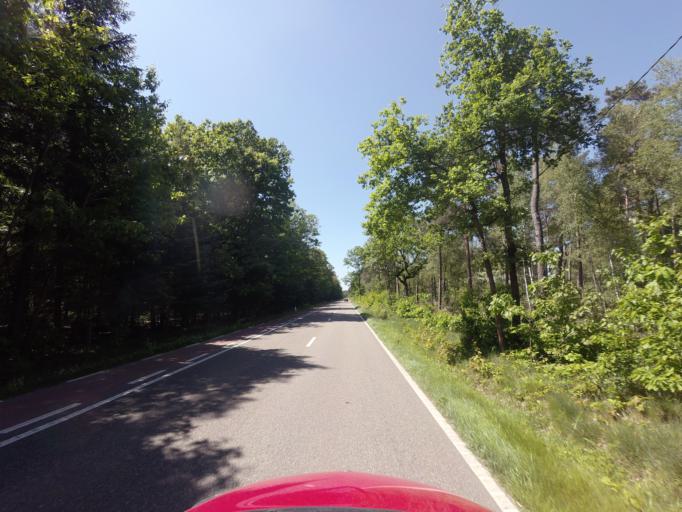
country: NL
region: North Brabant
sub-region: Gemeente Bladel en Netersel
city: Bladel
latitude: 51.2929
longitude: 5.2151
